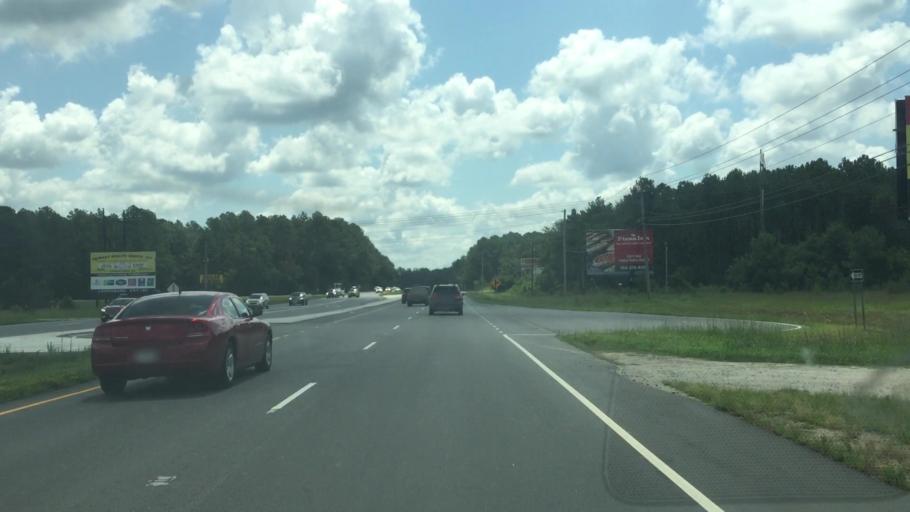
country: US
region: North Carolina
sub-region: Scotland County
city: Laurel Hill
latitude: 34.8035
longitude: -79.5397
